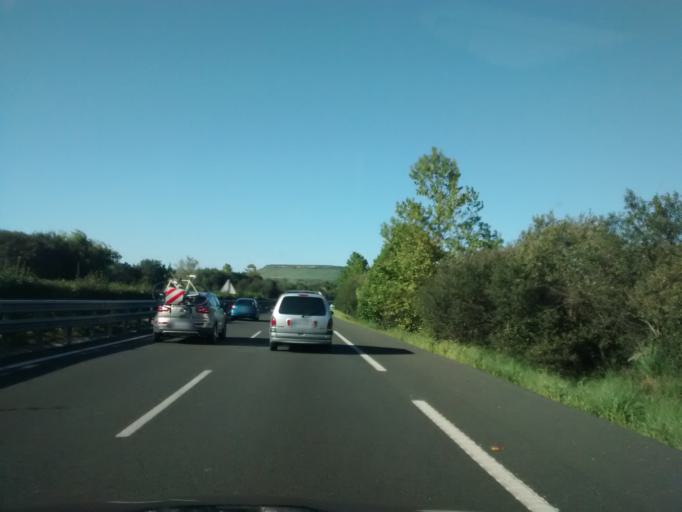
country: ES
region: Cantabria
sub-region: Provincia de Cantabria
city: Polanco
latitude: 43.3744
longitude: -4.0371
